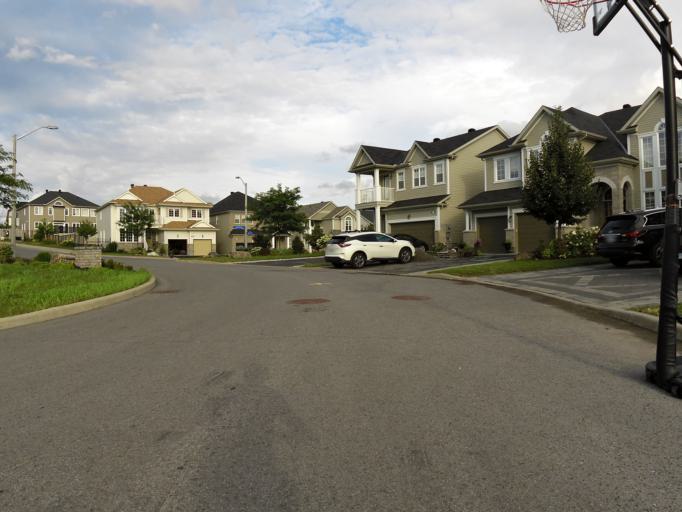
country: CA
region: Ontario
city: Bells Corners
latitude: 45.3149
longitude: -75.9367
